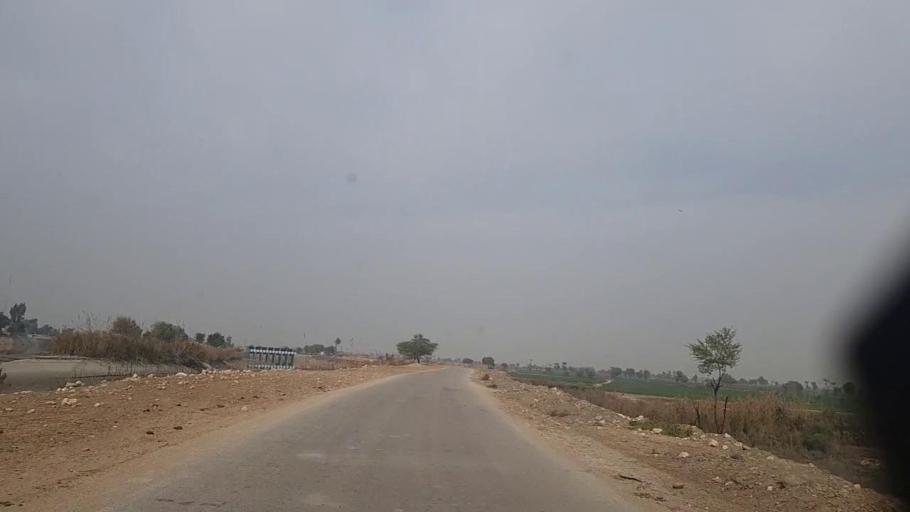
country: PK
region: Sindh
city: Sakrand
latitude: 26.2807
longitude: 68.2277
